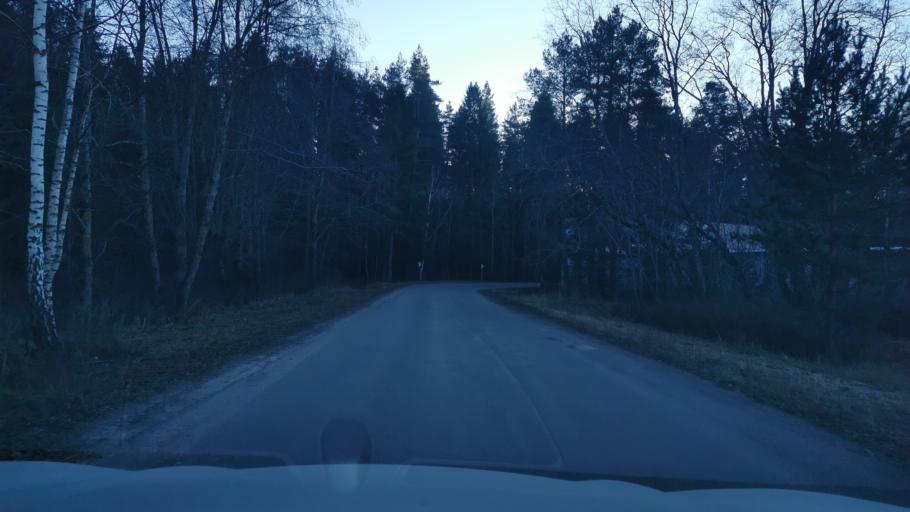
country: EE
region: Ida-Virumaa
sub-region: Kohtla-Nomme vald
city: Kohtla-Nomme
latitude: 59.3497
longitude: 27.1770
